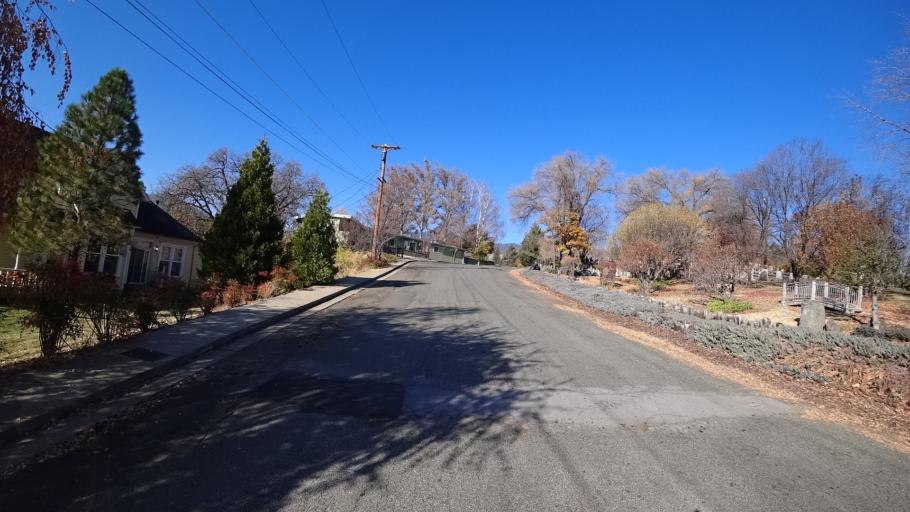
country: US
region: California
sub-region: Siskiyou County
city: Yreka
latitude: 41.7363
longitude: -122.6390
